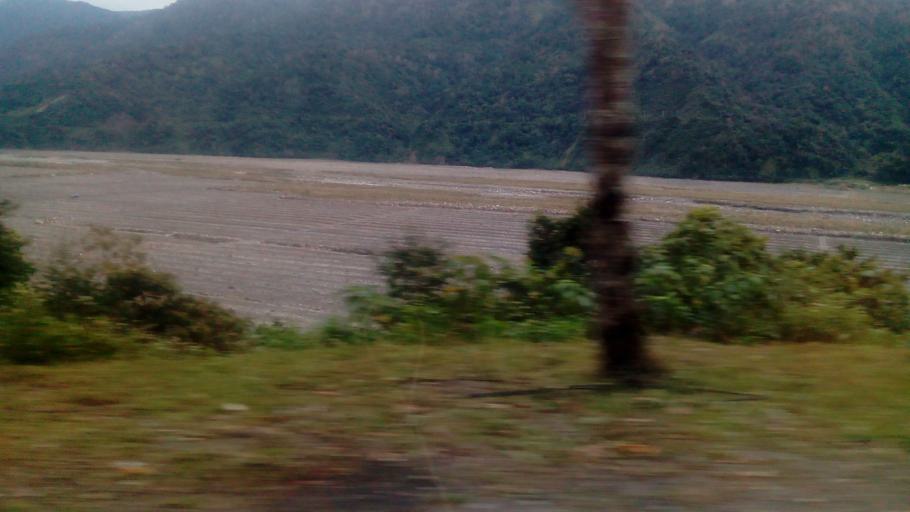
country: TW
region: Taiwan
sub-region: Yilan
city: Yilan
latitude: 24.5847
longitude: 121.4996
